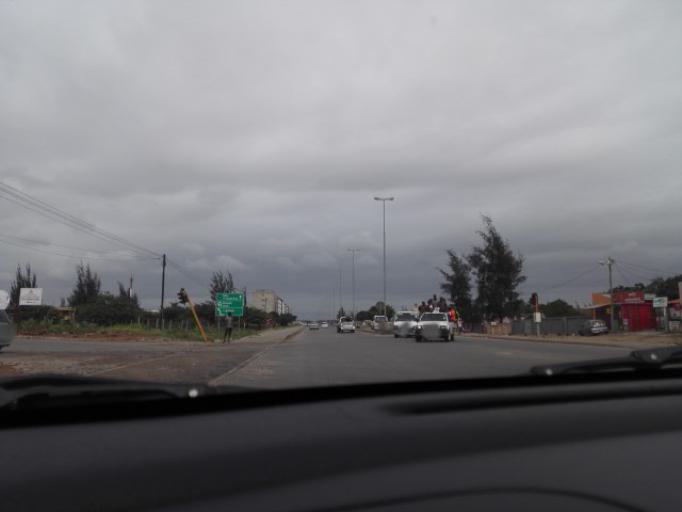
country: MZ
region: Maputo City
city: Maputo
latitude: -25.8209
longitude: 32.5833
